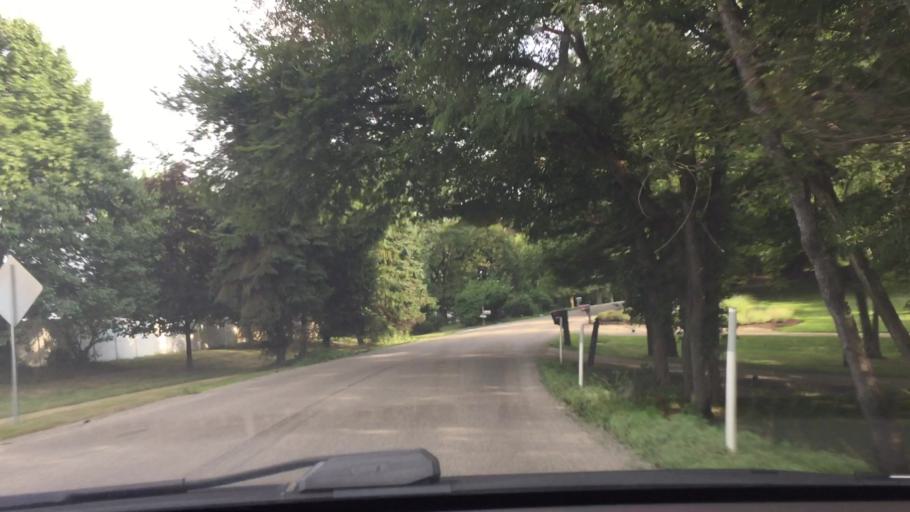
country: US
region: Pennsylvania
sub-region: Butler County
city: Seven Fields
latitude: 40.6755
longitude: -80.0684
